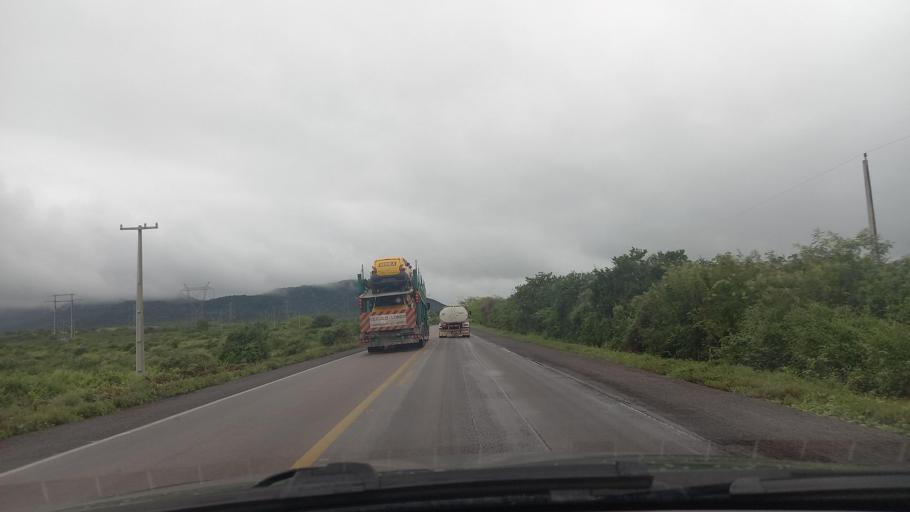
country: BR
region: Alagoas
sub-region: Agua Branca
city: Agua Branca
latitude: -9.3243
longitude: -37.9671
